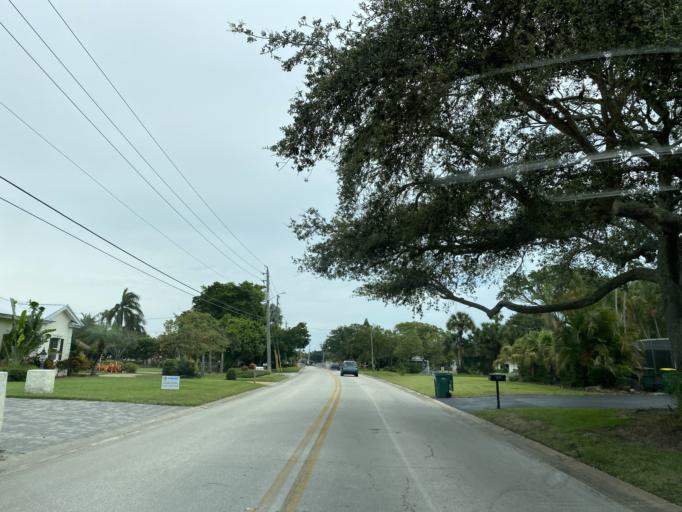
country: US
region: Florida
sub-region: Brevard County
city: Indialantic
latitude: 28.0859
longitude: -80.5743
